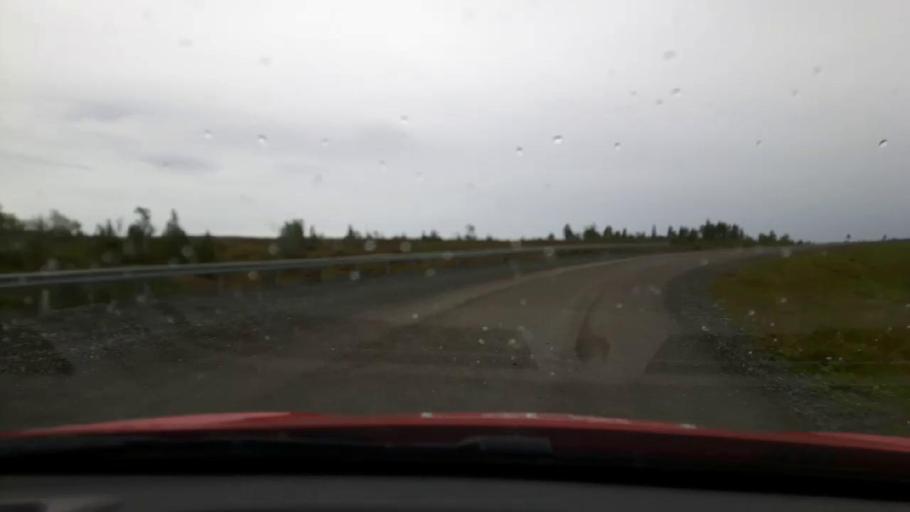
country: NO
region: Nord-Trondelag
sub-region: Meraker
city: Meraker
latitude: 63.6313
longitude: 12.2851
